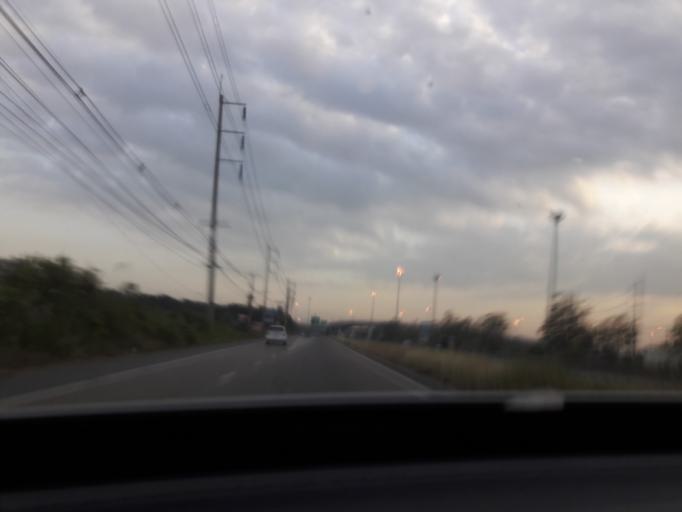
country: TH
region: Phra Nakhon Si Ayutthaya
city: Bang Pa-in
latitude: 14.1546
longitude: 100.5636
